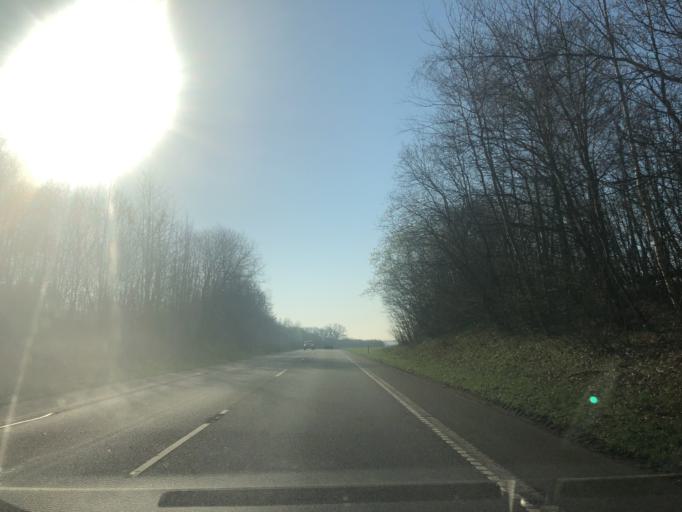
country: DK
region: Zealand
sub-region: Faxe Kommune
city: Ronnede
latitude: 55.2963
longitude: 12.0014
